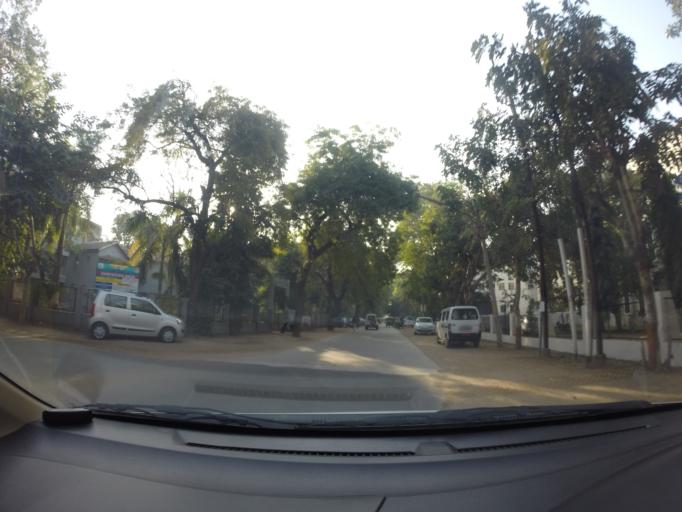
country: IN
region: Gujarat
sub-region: Anand
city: Karamsad
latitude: 22.5540
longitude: 72.9248
